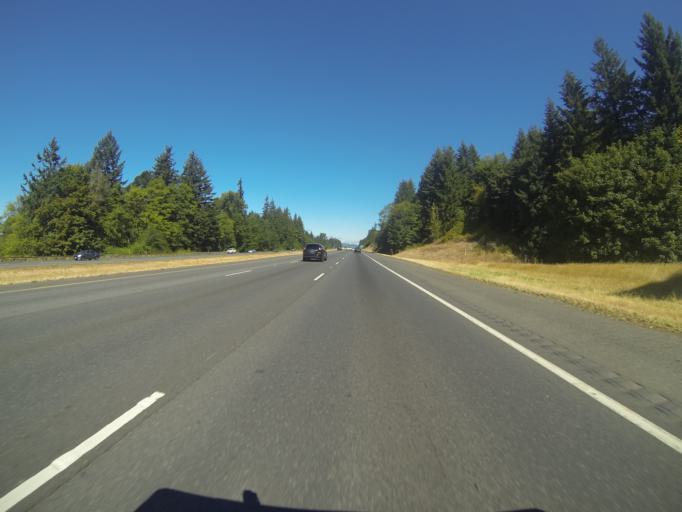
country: US
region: Washington
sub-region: Cowlitz County
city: Kalama
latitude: 45.9668
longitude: -122.8115
